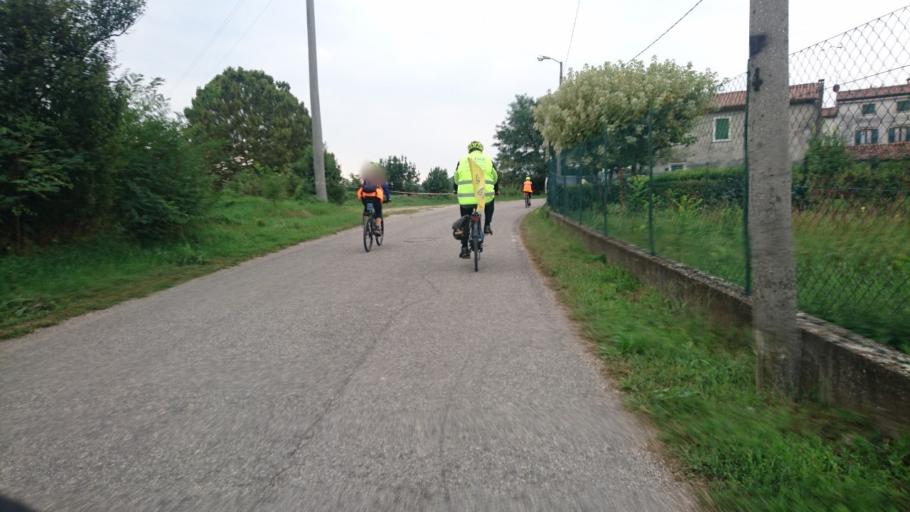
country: IT
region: Veneto
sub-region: Provincia di Verona
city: San Giovanni Lupatoto
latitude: 45.4122
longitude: 11.0593
